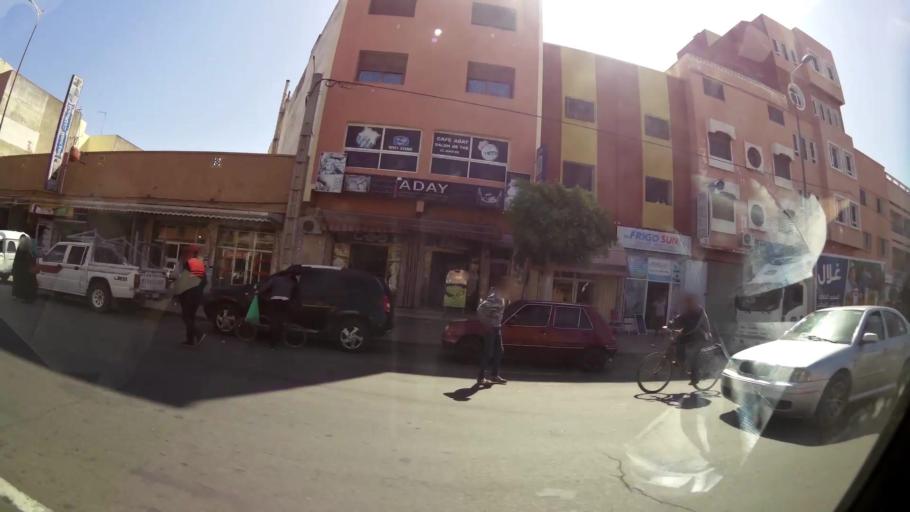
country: MA
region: Souss-Massa-Draa
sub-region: Inezgane-Ait Mellou
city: Inezgane
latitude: 30.3425
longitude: -9.5025
